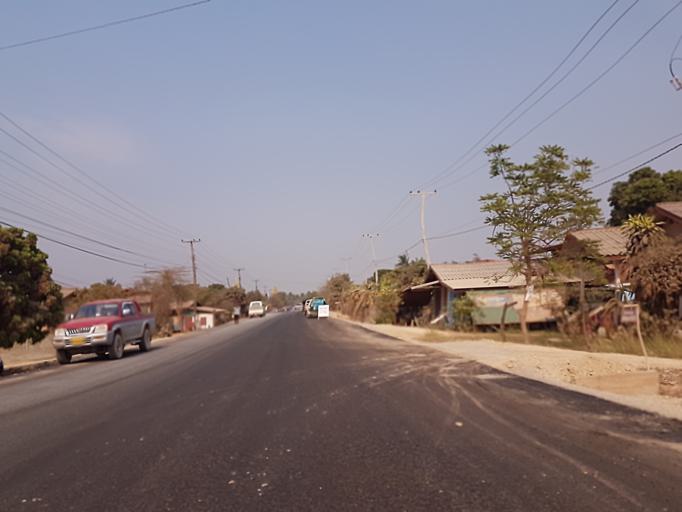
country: TH
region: Nong Khai
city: Nong Khai
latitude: 17.9325
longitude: 102.7788
